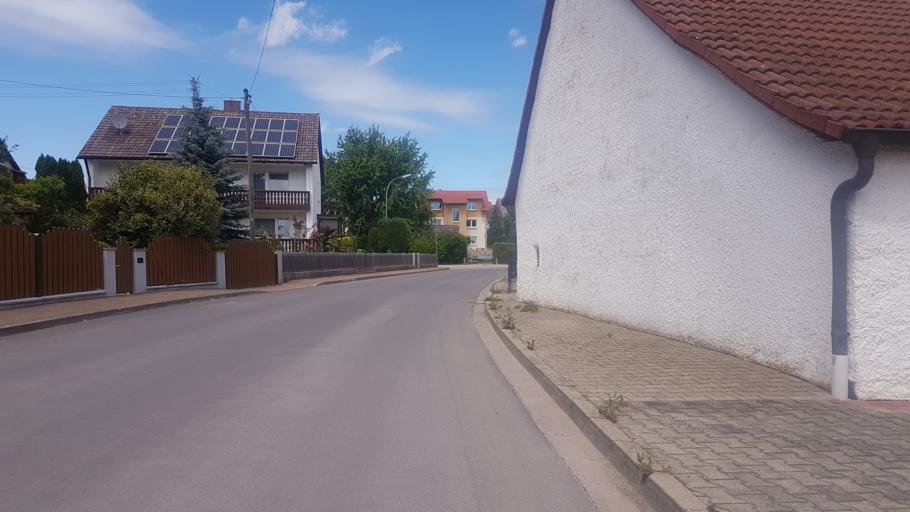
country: DE
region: Bavaria
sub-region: Swabia
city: Hochstadt an der Donau
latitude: 48.5948
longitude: 10.5421
